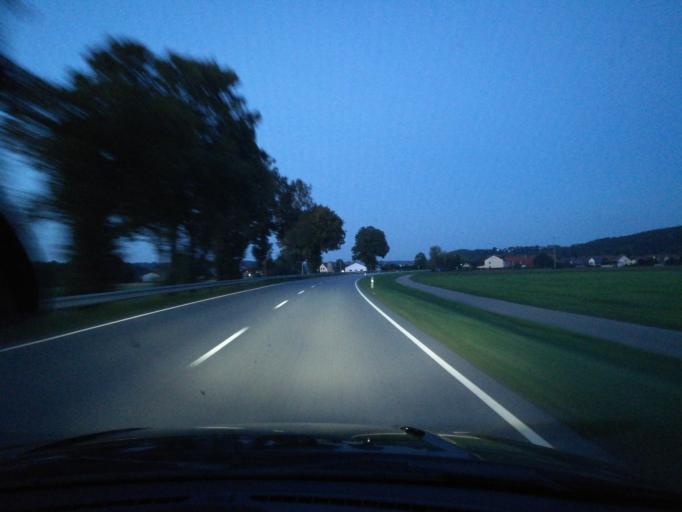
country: DE
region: Bavaria
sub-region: Lower Bavaria
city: Teugn
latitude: 48.9196
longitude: 11.9956
